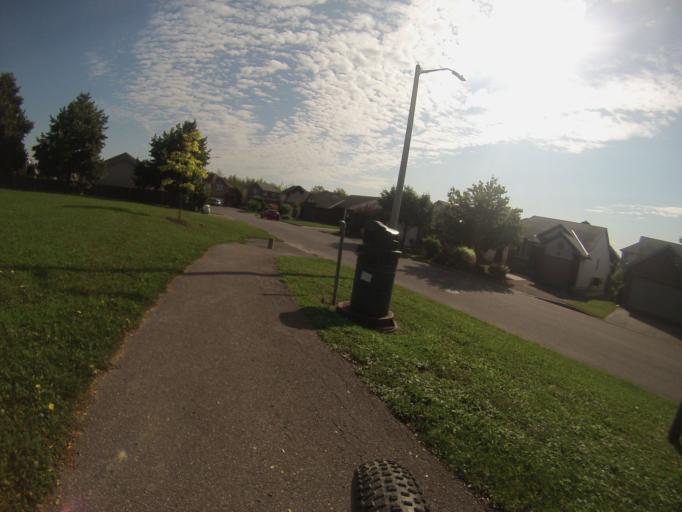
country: CA
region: Ontario
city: Ottawa
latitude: 45.3759
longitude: -75.6213
